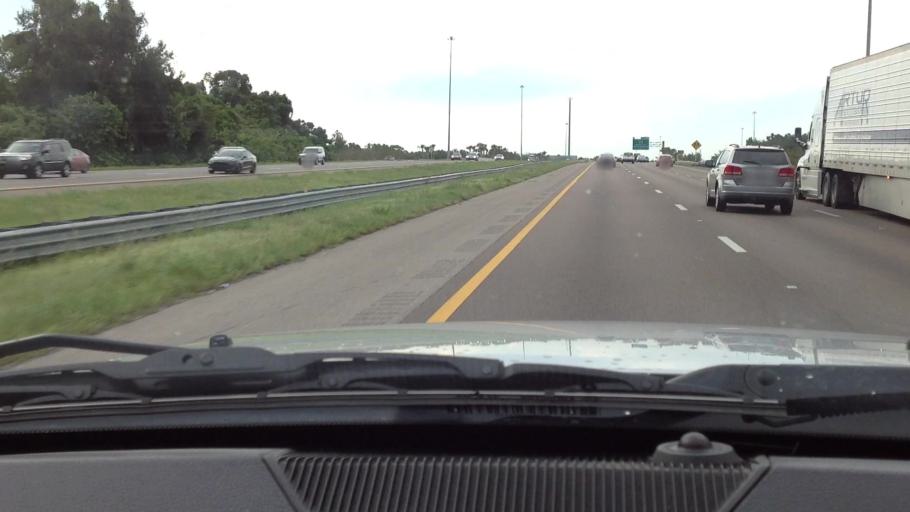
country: US
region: Florida
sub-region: Hillsborough County
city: Temple Terrace
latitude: 28.0526
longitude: -82.3543
